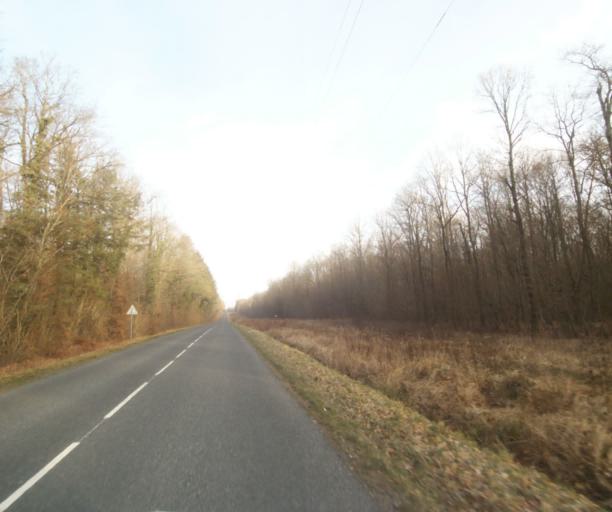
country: FR
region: Champagne-Ardenne
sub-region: Departement de la Haute-Marne
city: Bettancourt-la-Ferree
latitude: 48.6636
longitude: 4.9446
